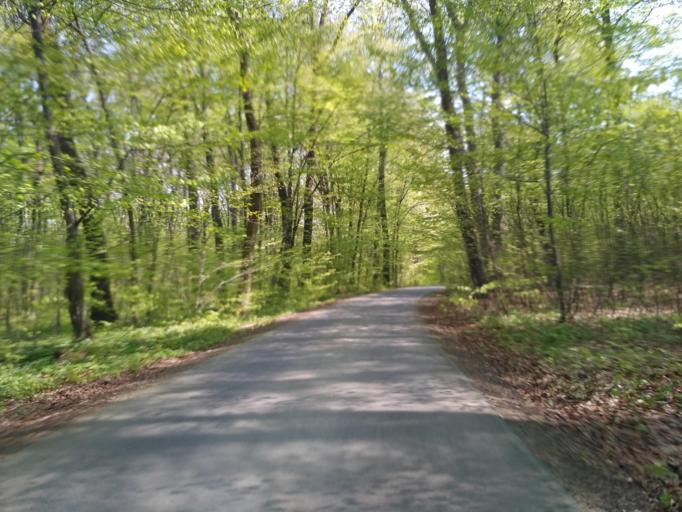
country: PL
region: Subcarpathian Voivodeship
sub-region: Powiat jasielski
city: Tarnowiec
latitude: 49.7396
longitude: 21.5955
